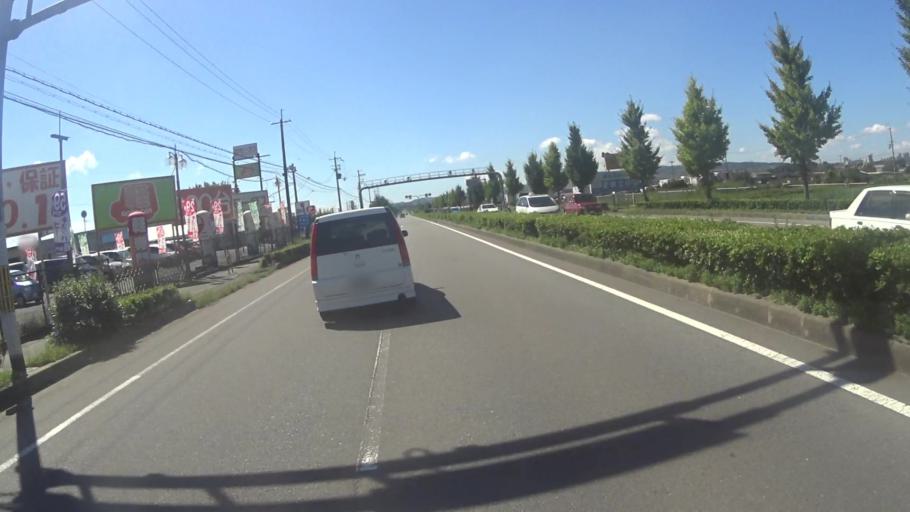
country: JP
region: Kyoto
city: Tanabe
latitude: 34.8589
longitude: 135.7623
